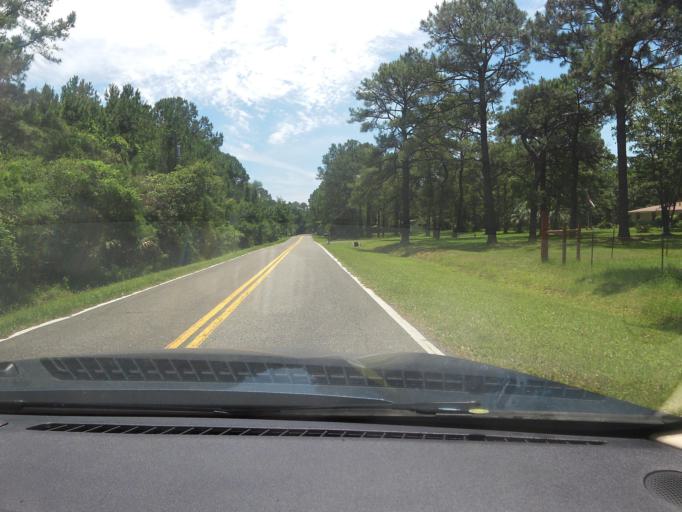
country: US
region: Florida
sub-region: Duval County
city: Atlantic Beach
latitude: 30.4549
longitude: -81.4669
